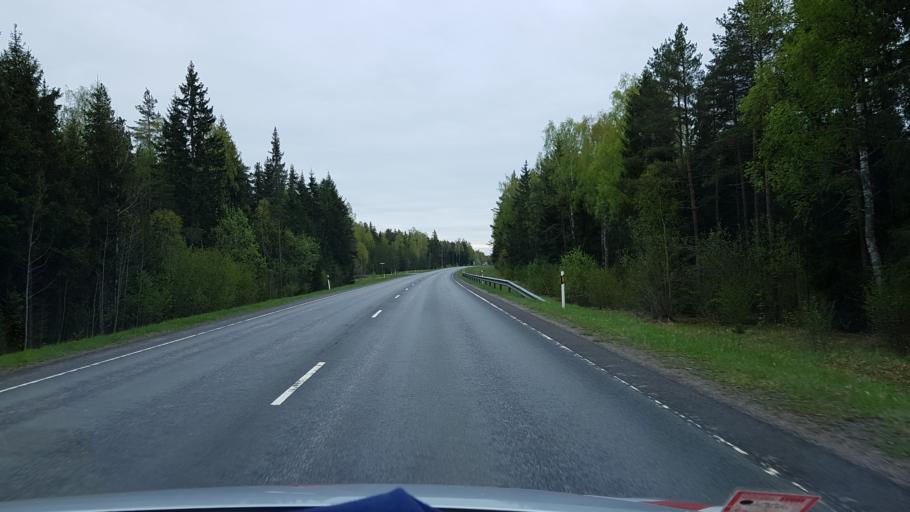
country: EE
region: Harju
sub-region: Nissi vald
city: Turba
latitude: 58.9689
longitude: 24.0659
